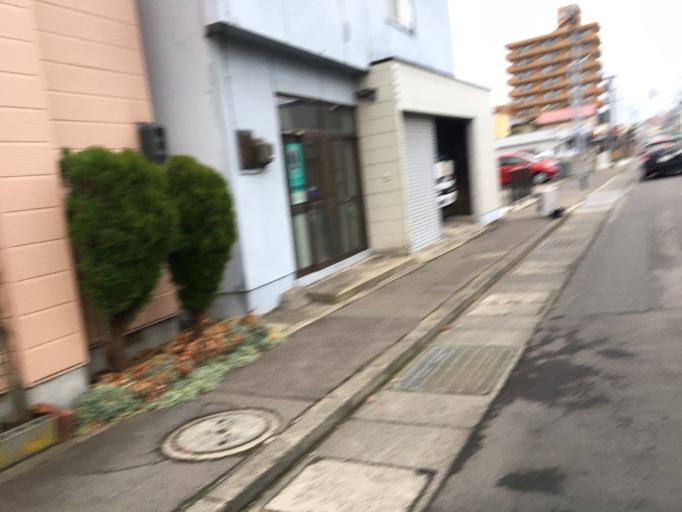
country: JP
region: Aomori
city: Hirosaki
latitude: 40.5943
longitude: 140.4778
